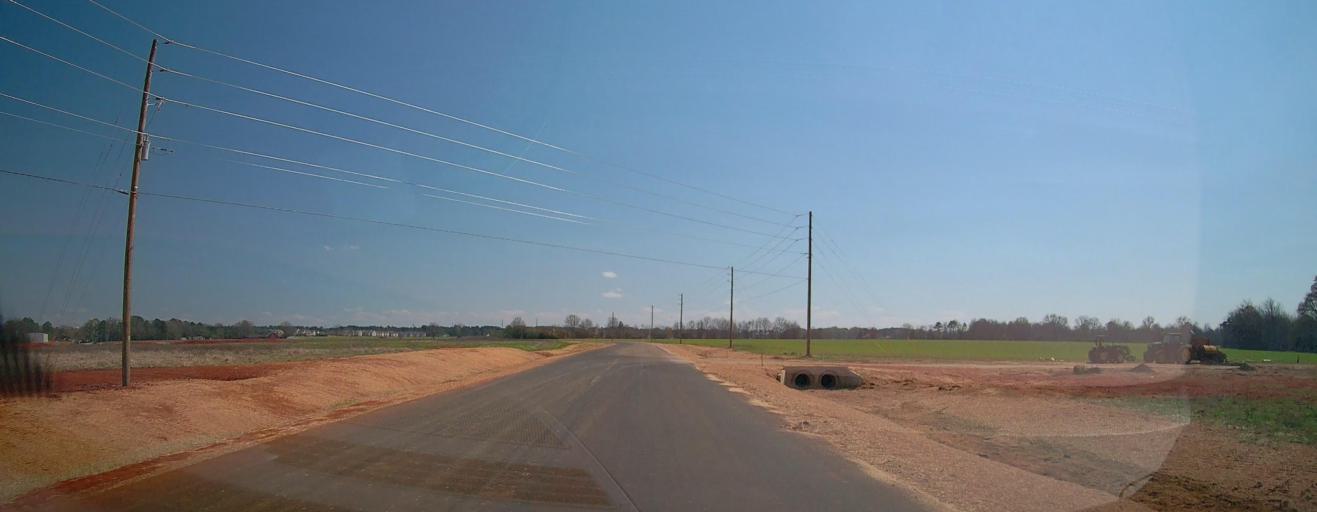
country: US
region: Georgia
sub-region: Houston County
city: Centerville
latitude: 32.5985
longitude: -83.7272
